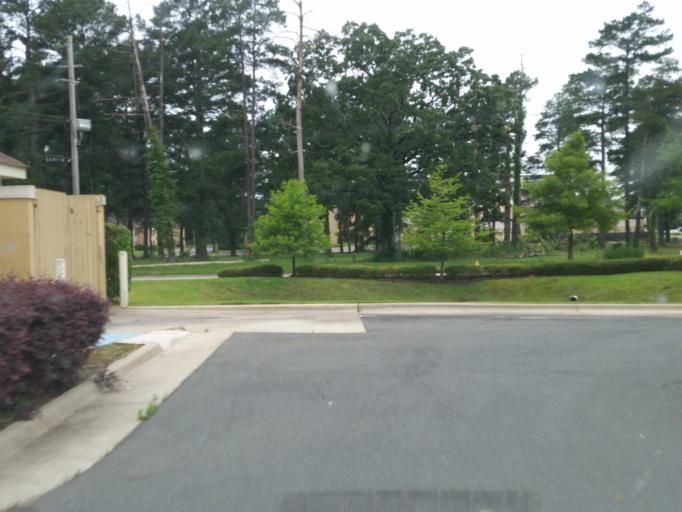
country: US
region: Louisiana
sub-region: Caddo Parish
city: Shreveport
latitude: 32.4525
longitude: -93.8458
